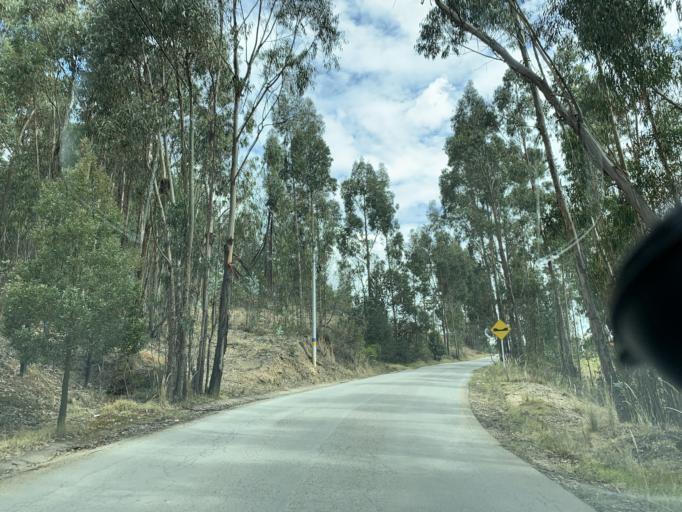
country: CO
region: Boyaca
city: Siachoque
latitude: 5.5706
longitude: -73.2672
